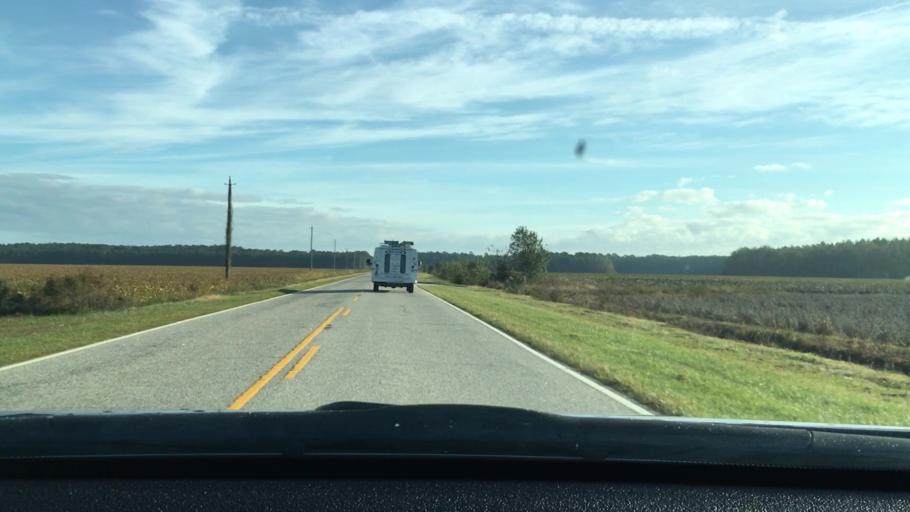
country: US
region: South Carolina
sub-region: Lee County
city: Bishopville
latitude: 34.0806
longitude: -80.1974
